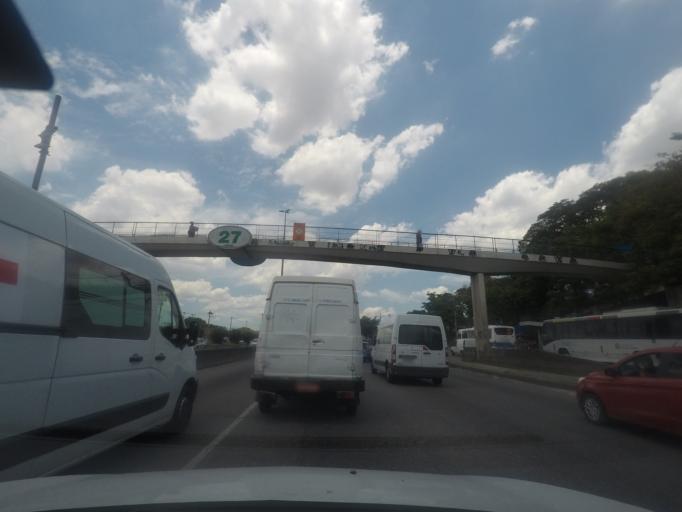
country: BR
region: Rio de Janeiro
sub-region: Sao Joao De Meriti
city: Sao Joao de Meriti
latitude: -22.8263
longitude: -43.3385
